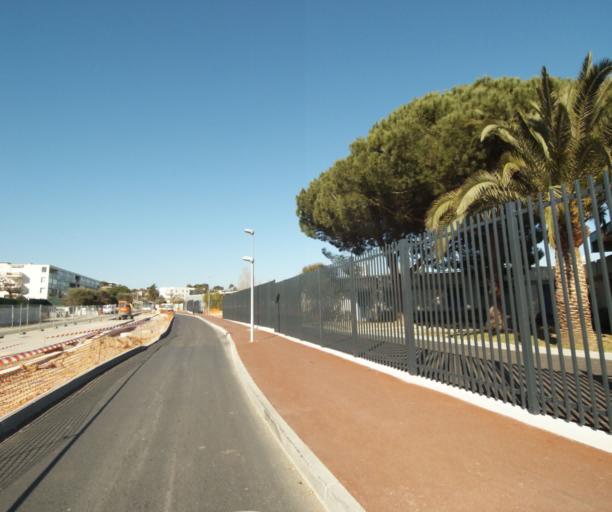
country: FR
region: Provence-Alpes-Cote d'Azur
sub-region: Departement des Alpes-Maritimes
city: Antibes
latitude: 43.5929
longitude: 7.1140
